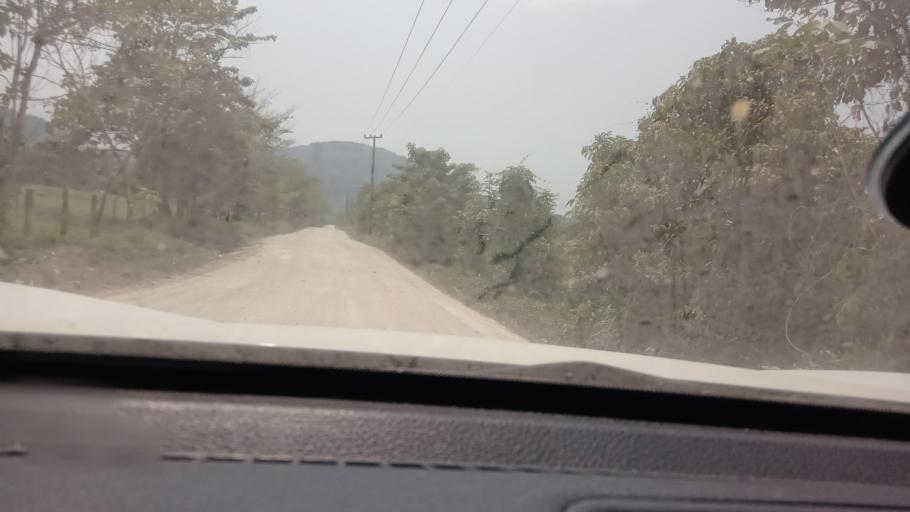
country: MX
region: Chiapas
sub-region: Tecpatan
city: Raudales Malpaso
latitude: 17.4744
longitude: -93.8228
